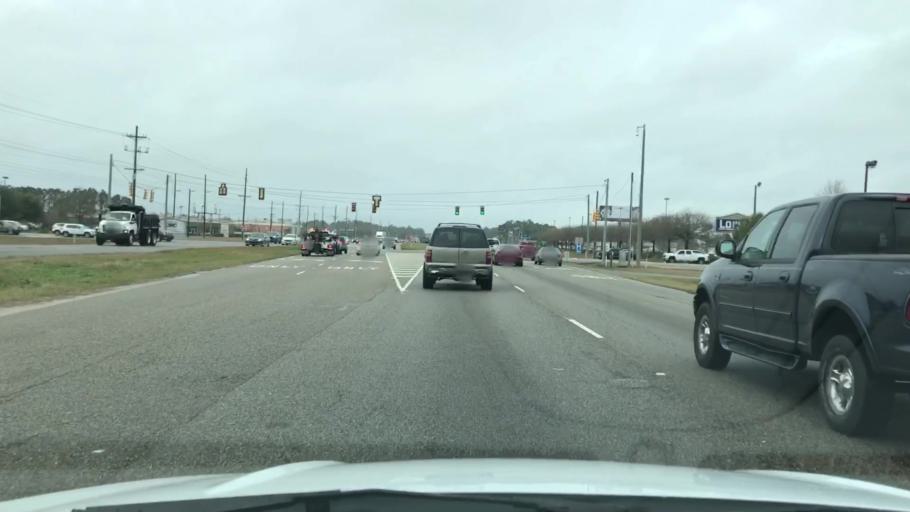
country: US
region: South Carolina
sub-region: Horry County
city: Red Hill
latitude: 33.7899
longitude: -78.9961
